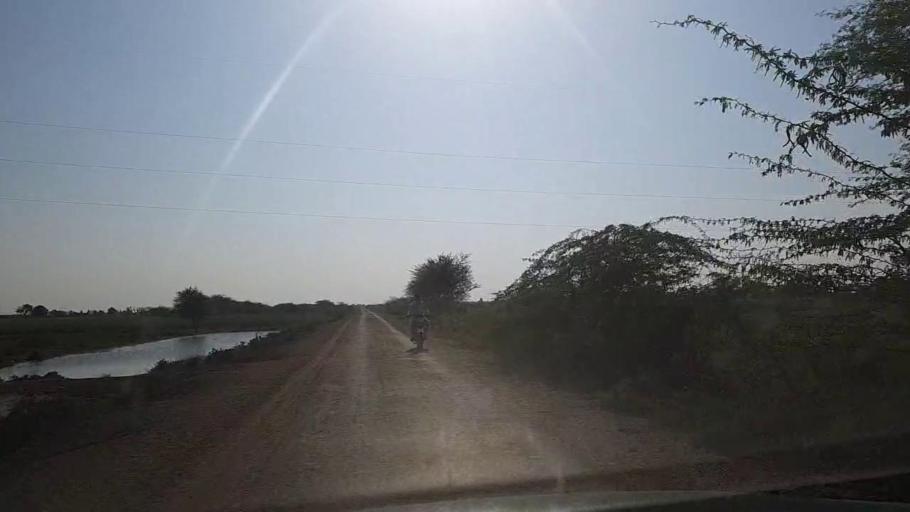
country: PK
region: Sindh
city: Digri
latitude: 25.0435
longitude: 69.2293
